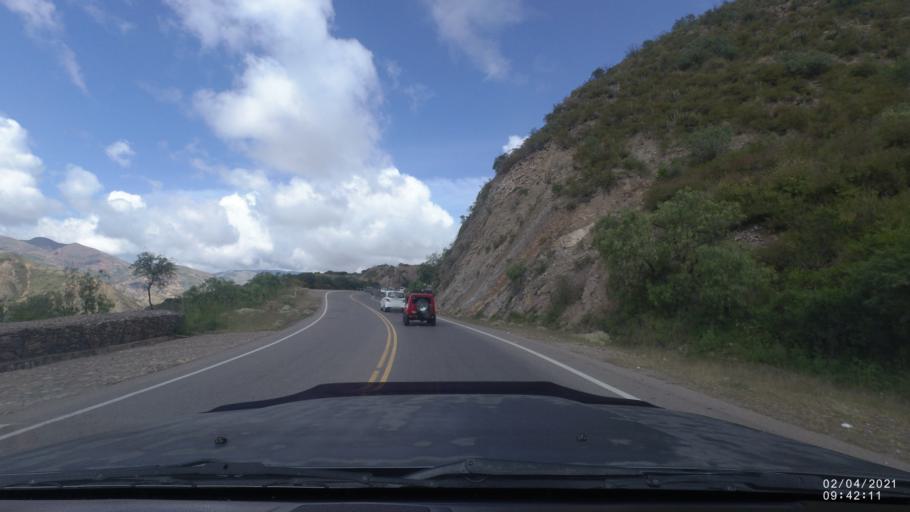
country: BO
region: Cochabamba
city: Irpa Irpa
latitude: -17.6346
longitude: -66.3678
